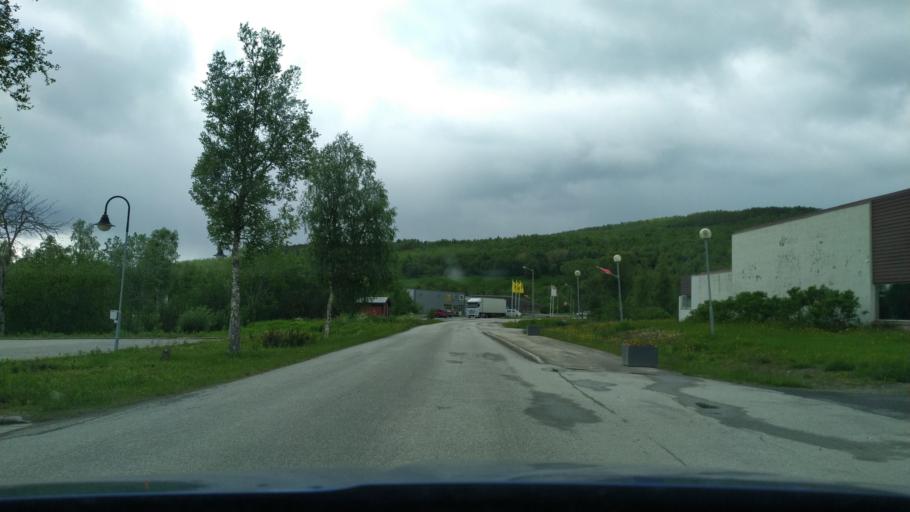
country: NO
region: Troms
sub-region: Dyroy
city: Brostadbotn
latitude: 69.0906
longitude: 17.6984
